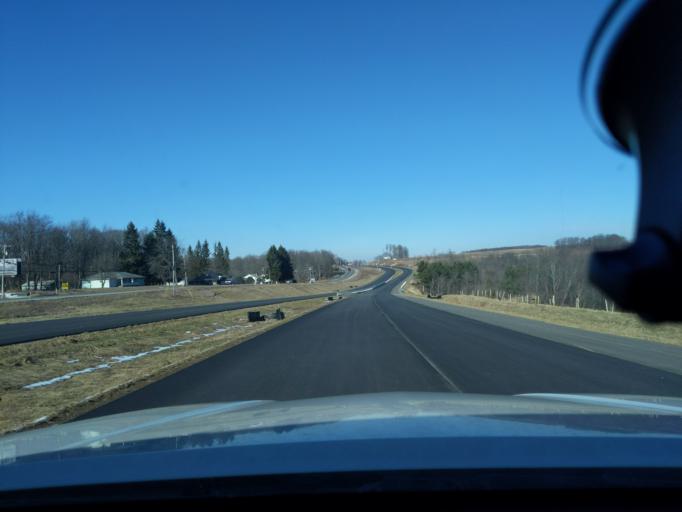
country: US
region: Pennsylvania
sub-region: Somerset County
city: Meyersdale
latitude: 39.6965
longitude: -79.0983
